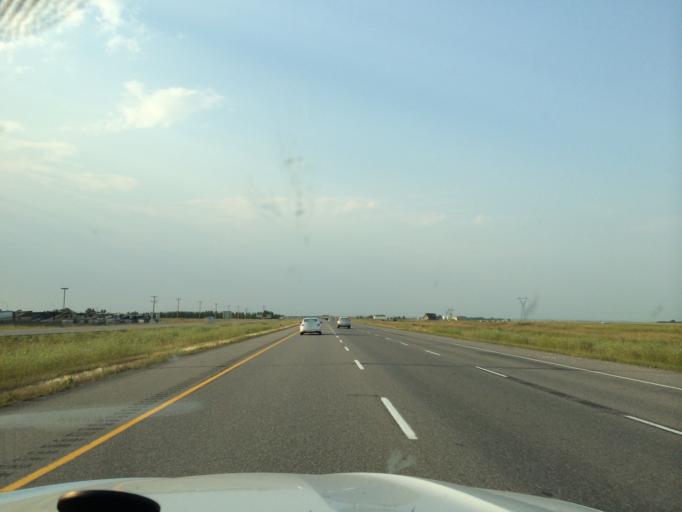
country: CA
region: Alberta
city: High River
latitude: 50.5807
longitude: -113.8281
